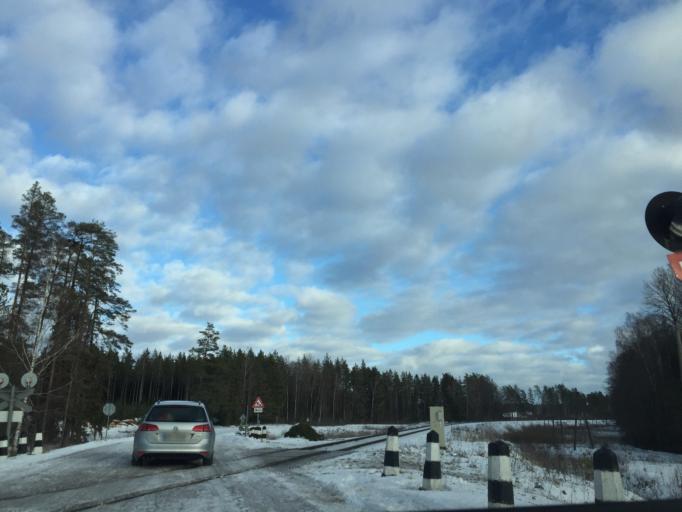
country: LV
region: Ogre
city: Jumprava
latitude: 56.5622
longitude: 24.9119
